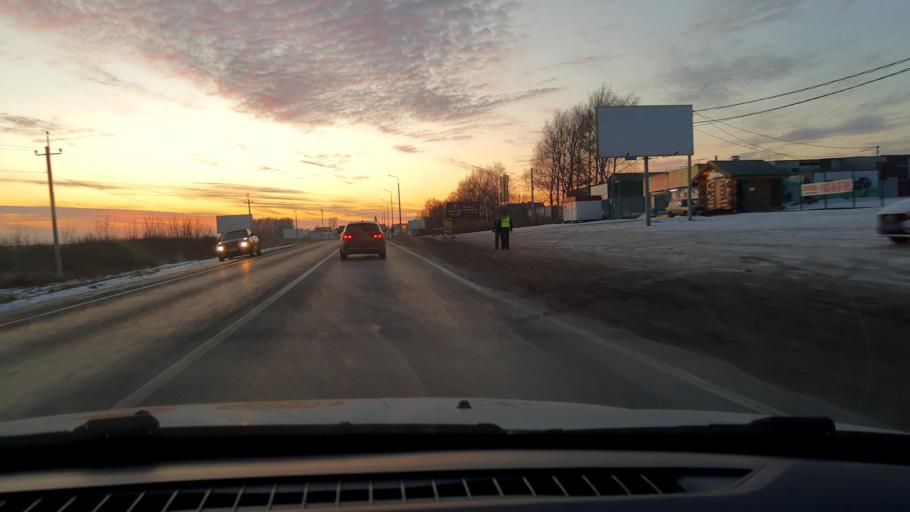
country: RU
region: Nizjnij Novgorod
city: Burevestnik
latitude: 56.2135
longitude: 43.8985
